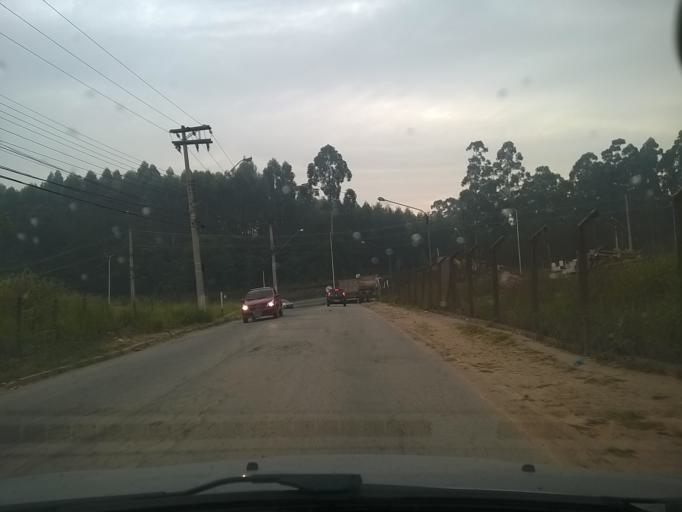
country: BR
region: Sao Paulo
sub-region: Caieiras
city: Caieiras
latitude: -23.3803
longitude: -46.7403
